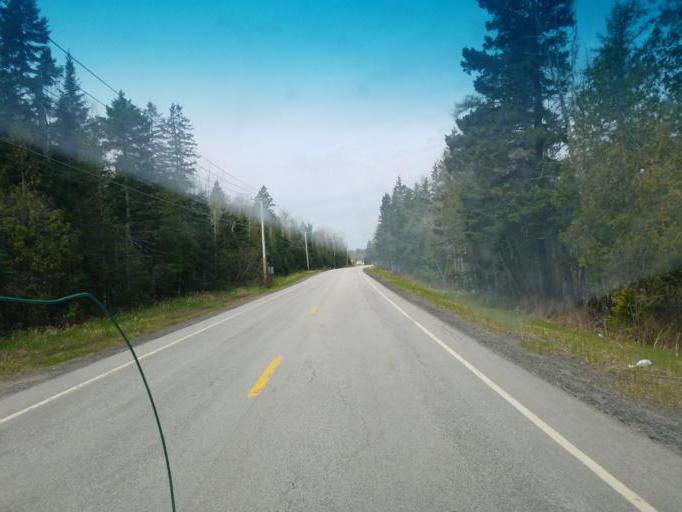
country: US
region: Maine
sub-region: Washington County
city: Eastport
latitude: 44.8011
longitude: -67.1311
